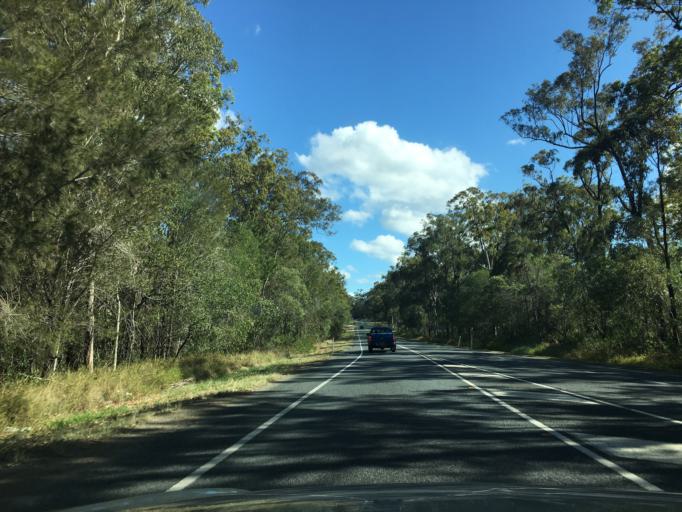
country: AU
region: Queensland
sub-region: Logan
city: Chambers Flat
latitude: -27.7886
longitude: 153.1005
